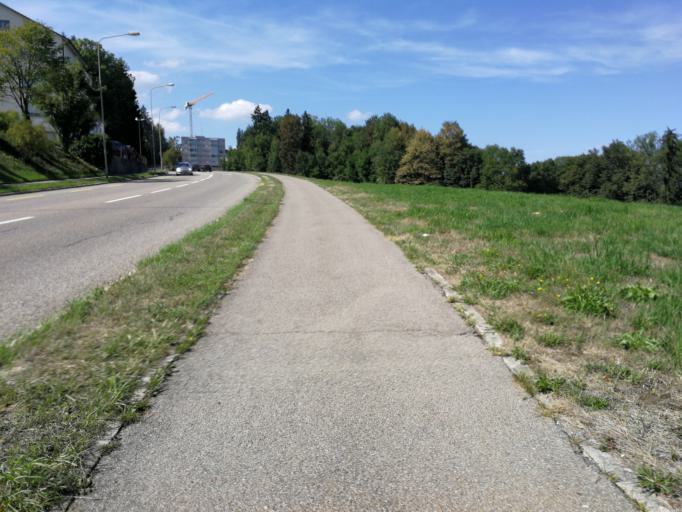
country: CH
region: Zurich
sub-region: Bezirk Horgen
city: Waedenswil / Hangenmoos
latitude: 47.2365
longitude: 8.6498
